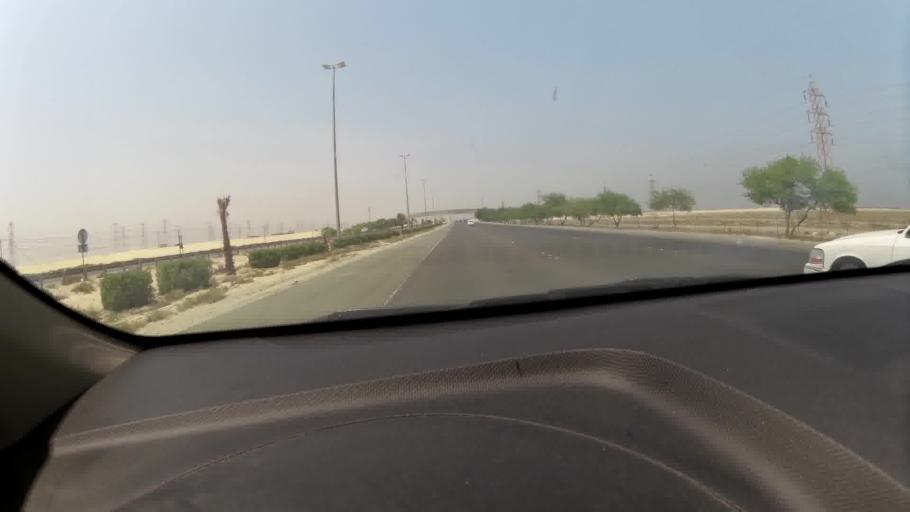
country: KW
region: Al Ahmadi
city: Al Fahahil
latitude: 28.8601
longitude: 48.2398
